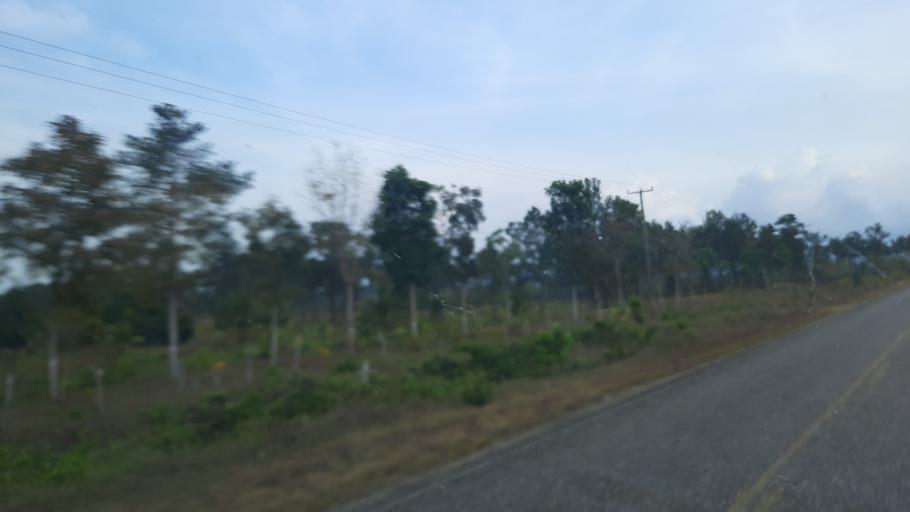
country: BZ
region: Stann Creek
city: Placencia
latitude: 16.5970
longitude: -88.5168
